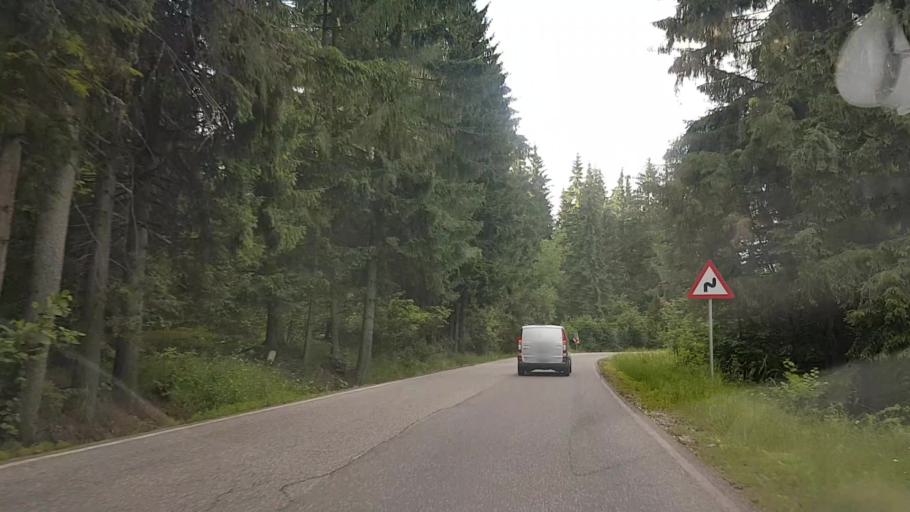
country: RO
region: Harghita
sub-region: Comuna Remetea
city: Remetea
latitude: 46.6768
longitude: 25.3650
